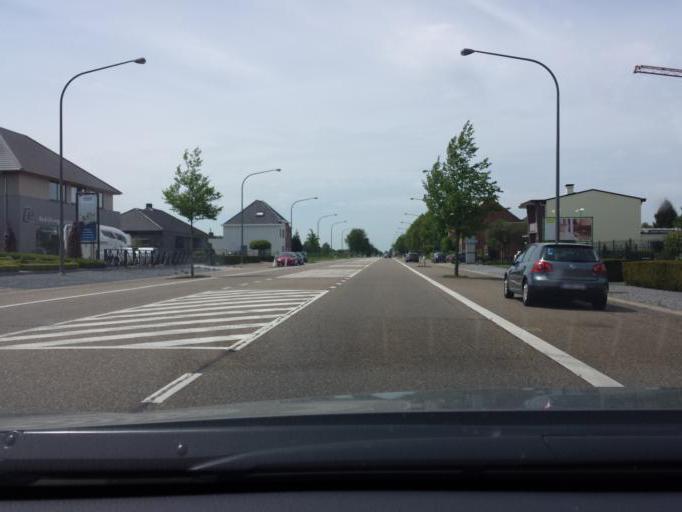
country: BE
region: Flanders
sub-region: Provincie Limburg
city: Lummen
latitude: 50.9477
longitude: 5.2447
